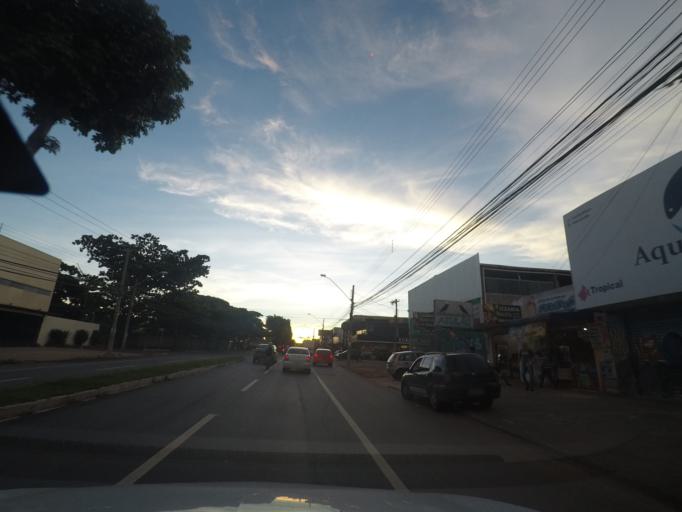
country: BR
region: Goias
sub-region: Goiania
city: Goiania
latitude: -16.6958
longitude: -49.2986
